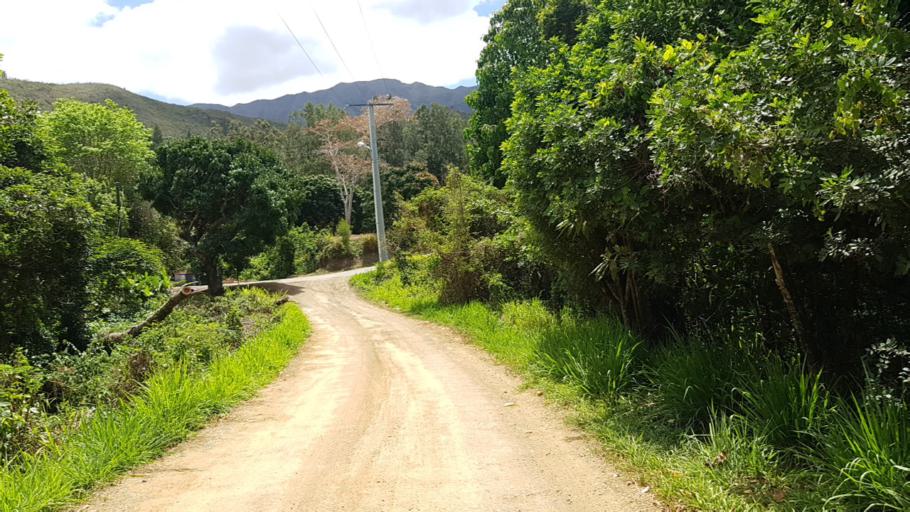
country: NC
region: South Province
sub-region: Dumbea
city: Dumbea
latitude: -22.1803
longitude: 166.4826
